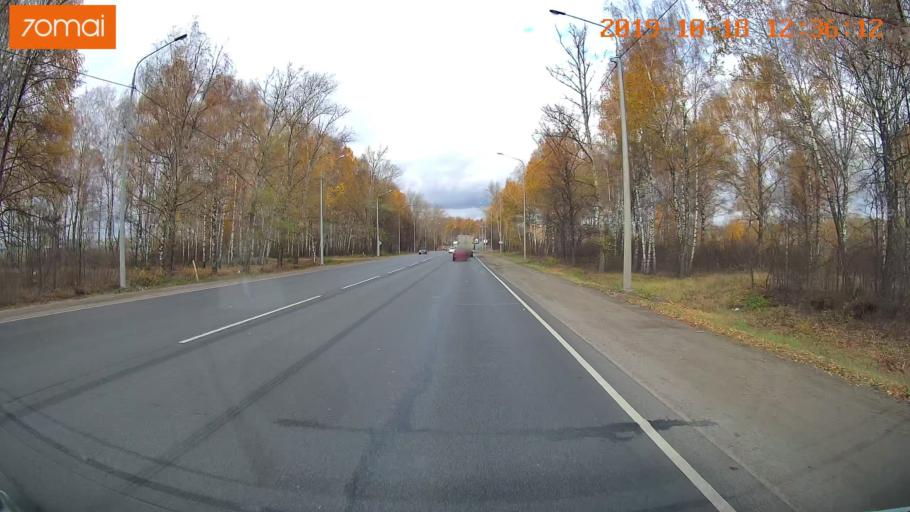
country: RU
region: Rjazan
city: Ryazan'
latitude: 54.6326
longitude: 39.6343
